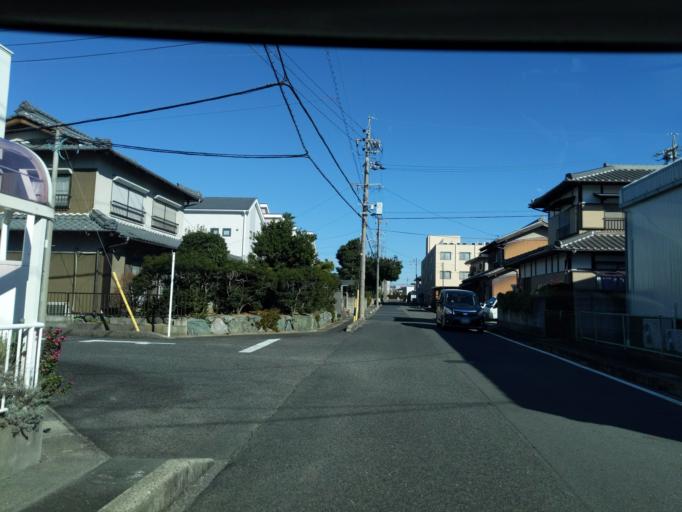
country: JP
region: Aichi
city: Kasugai
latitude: 35.2542
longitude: 136.9723
